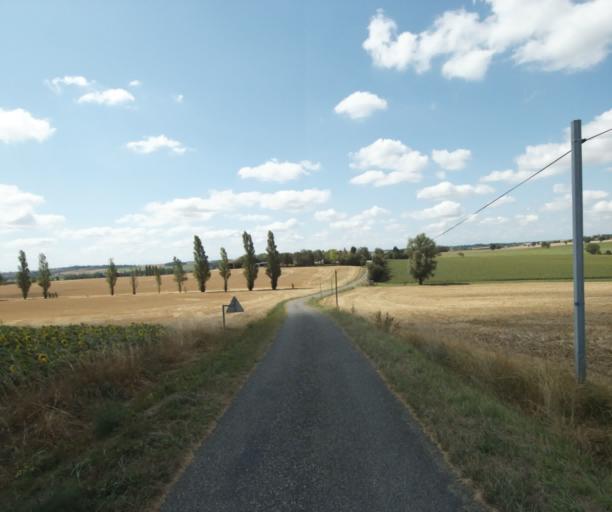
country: FR
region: Midi-Pyrenees
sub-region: Departement de la Haute-Garonne
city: Auriac-sur-Vendinelle
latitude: 43.4578
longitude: 1.8048
